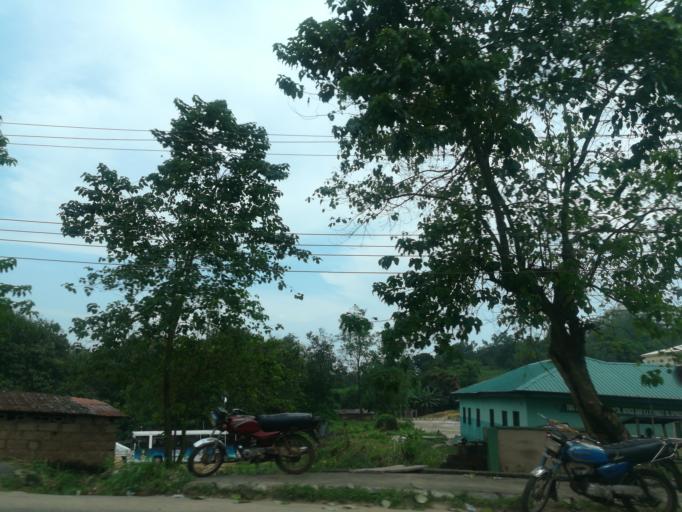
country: NG
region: Oyo
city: Ibadan
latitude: 7.4121
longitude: 3.8939
